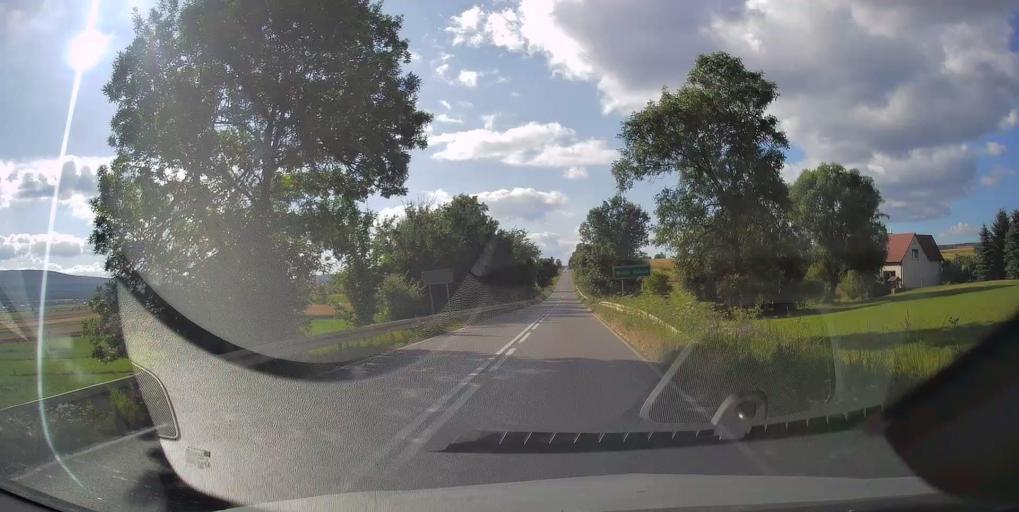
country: PL
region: Swietokrzyskie
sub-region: Powiat kielecki
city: Bodzentyn
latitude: 50.9676
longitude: 20.8887
